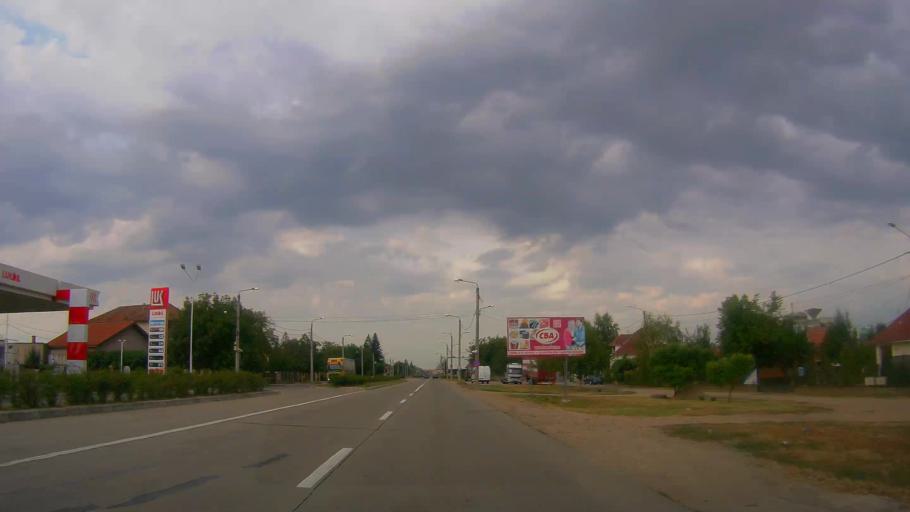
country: RO
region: Satu Mare
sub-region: Comuna Paulesti
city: Paulesti
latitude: 47.8069
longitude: 22.9143
